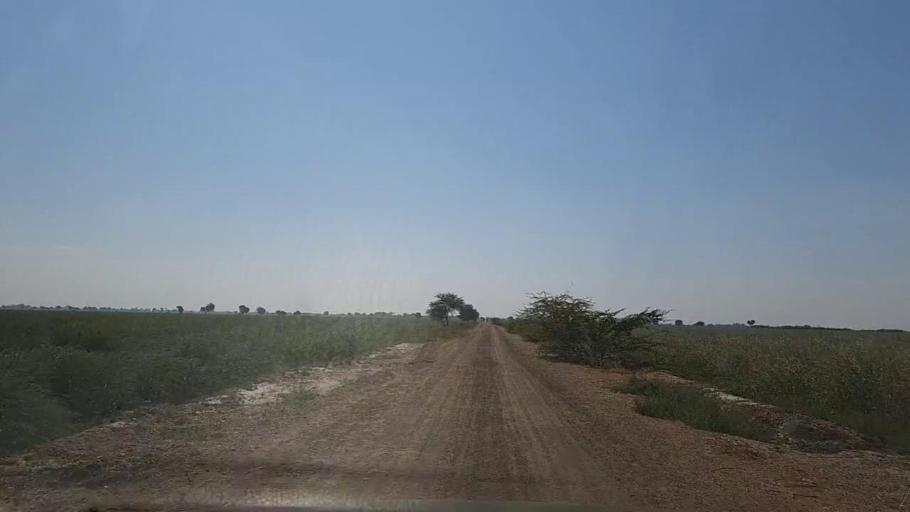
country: PK
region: Sindh
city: Pithoro
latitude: 25.4192
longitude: 69.3799
